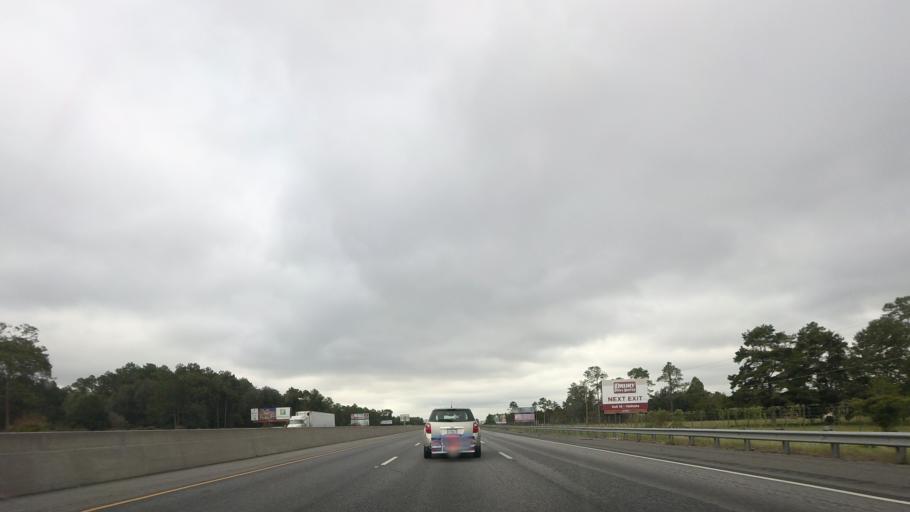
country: US
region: Georgia
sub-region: Lowndes County
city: Remerton
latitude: 30.8825
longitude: -83.3475
